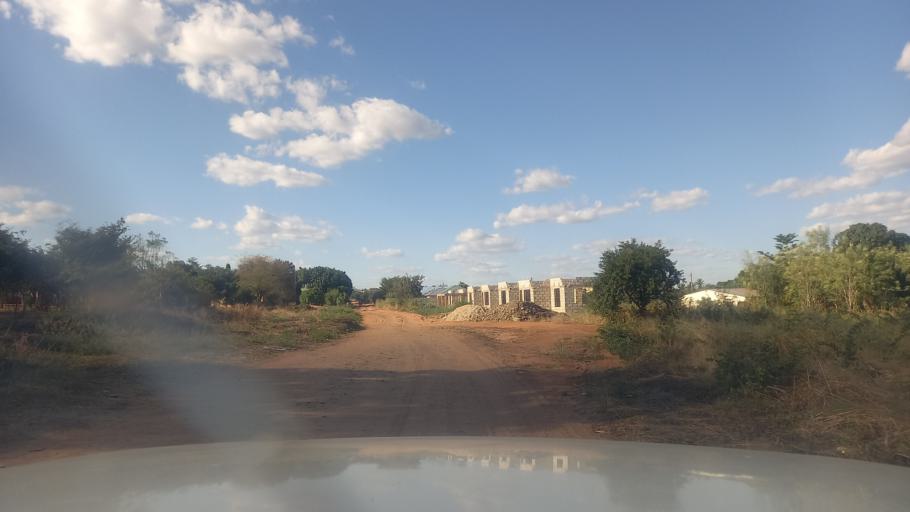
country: ZM
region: Southern
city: Livingstone
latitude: -17.8286
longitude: 25.8687
